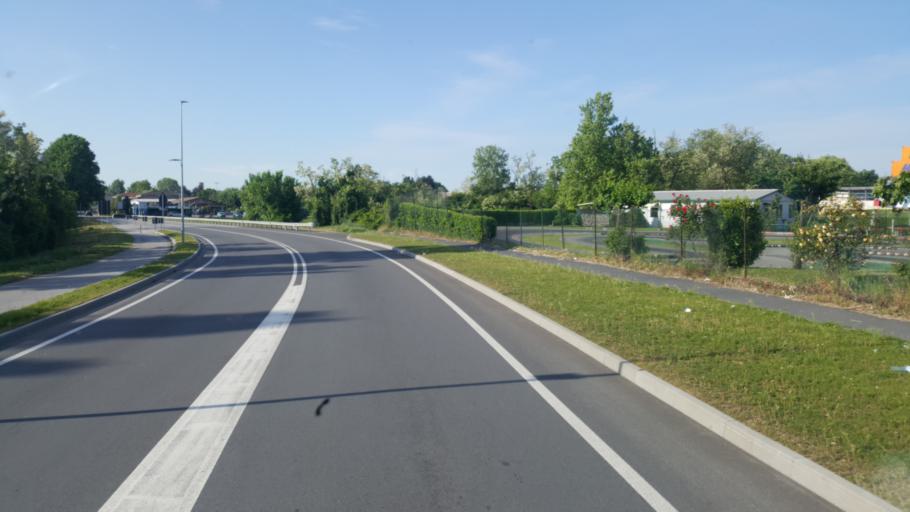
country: IT
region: Lombardy
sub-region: Citta metropolitana di Milano
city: Liscate
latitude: 45.4925
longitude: 9.4080
